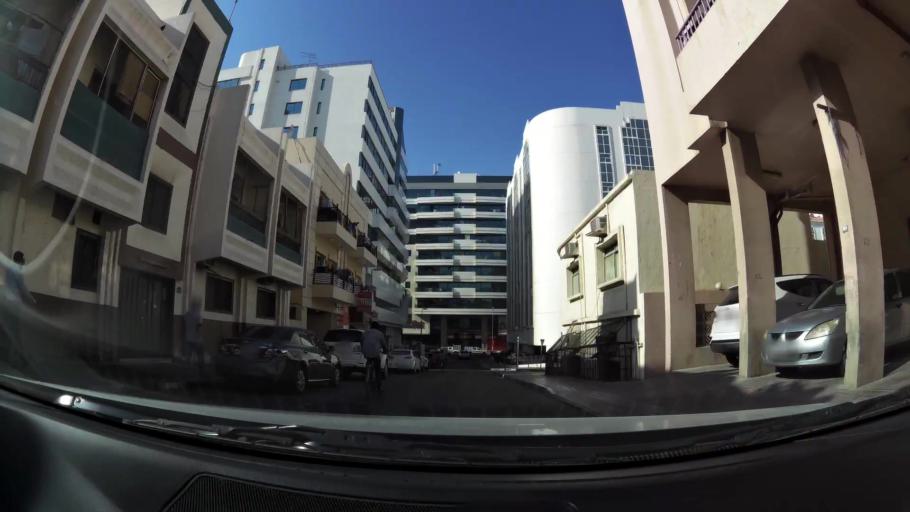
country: AE
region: Ash Shariqah
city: Sharjah
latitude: 25.2577
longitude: 55.2944
